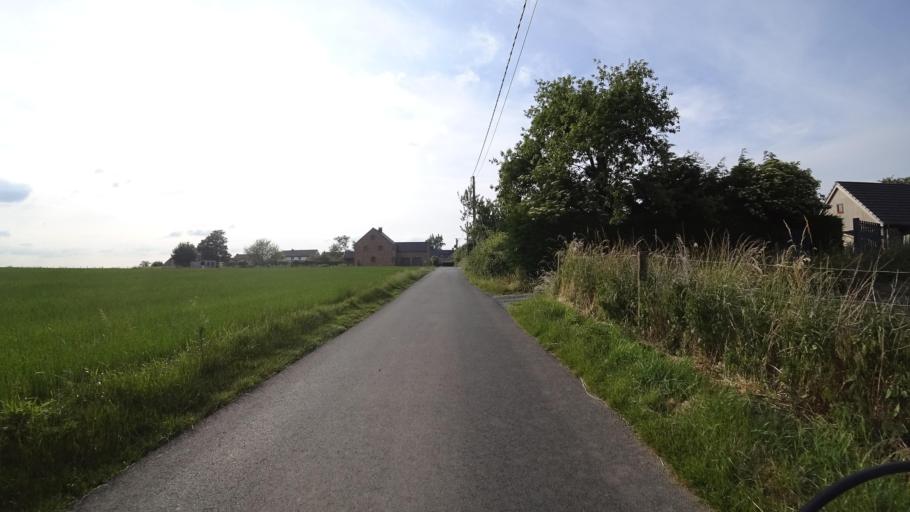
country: BE
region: Wallonia
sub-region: Province du Brabant Wallon
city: Perwez
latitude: 50.5514
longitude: 4.7845
